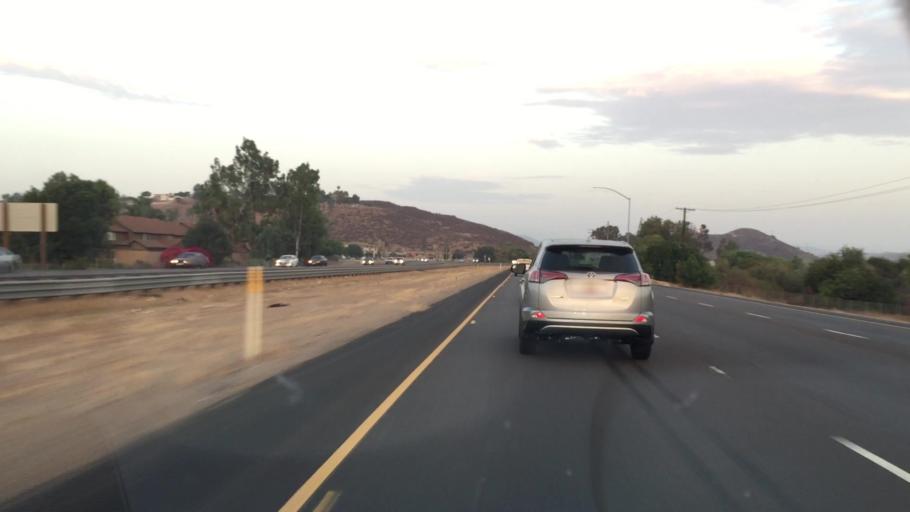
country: US
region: California
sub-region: San Diego County
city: Lakeside
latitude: 32.8574
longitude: -116.9350
